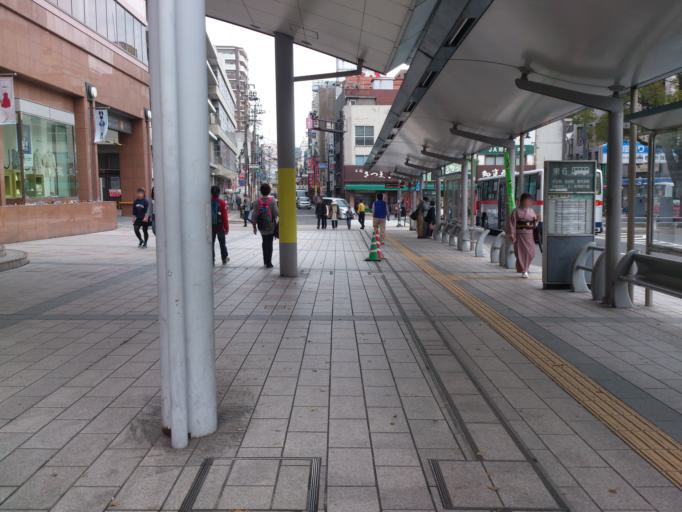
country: JP
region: Kagoshima
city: Kagoshima-shi
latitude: 31.5847
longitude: 130.5433
